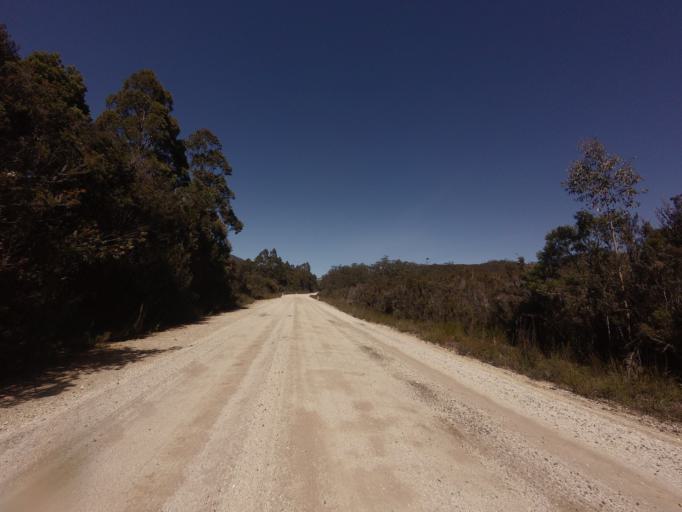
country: AU
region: Tasmania
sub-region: Huon Valley
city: Geeveston
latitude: -42.9007
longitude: 146.3731
